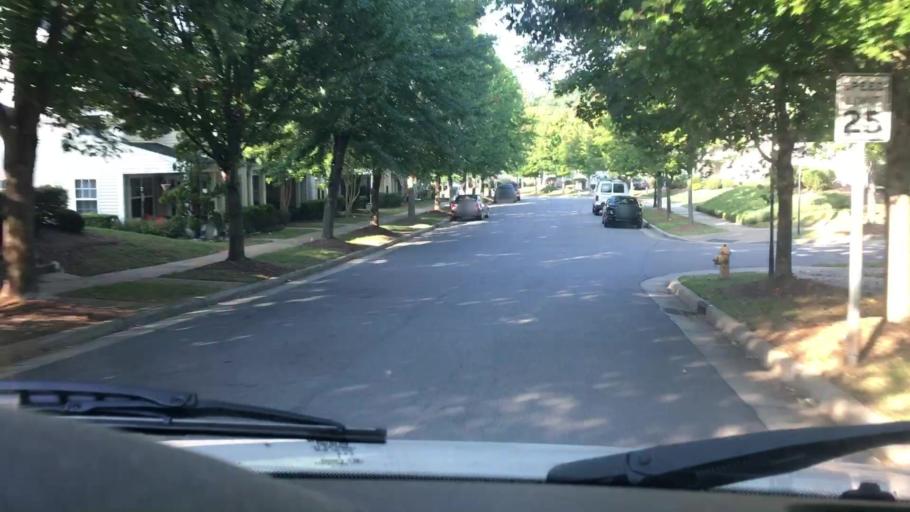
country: US
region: North Carolina
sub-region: Mecklenburg County
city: Cornelius
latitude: 35.4513
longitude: -80.8478
